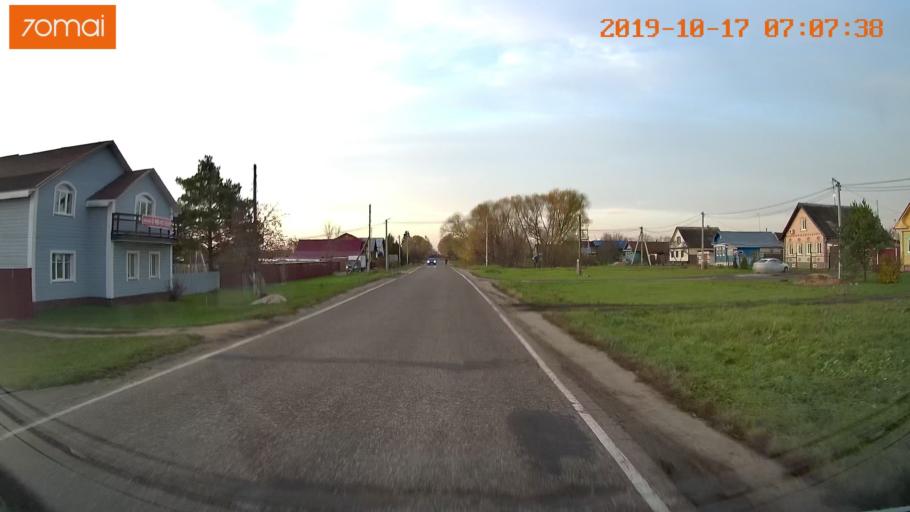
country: RU
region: Vladimir
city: Suzdal'
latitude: 56.4271
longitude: 40.4160
